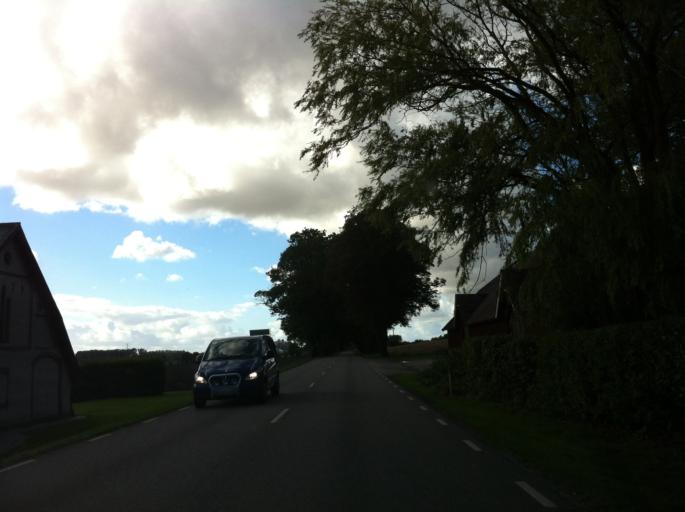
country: SE
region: Skane
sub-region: Eslovs Kommun
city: Eslov
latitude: 55.7797
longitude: 13.2932
